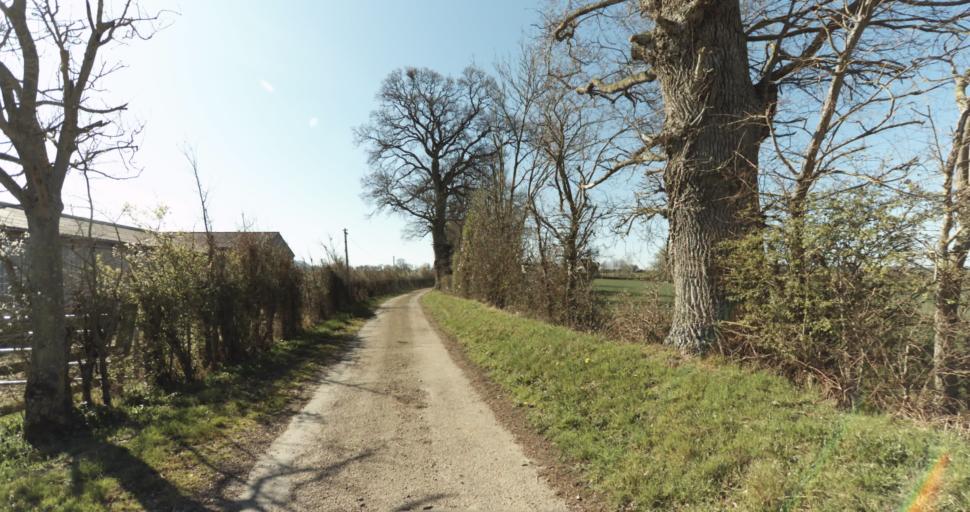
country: FR
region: Lower Normandy
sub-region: Departement de l'Orne
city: Trun
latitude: 48.9261
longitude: 0.0383
